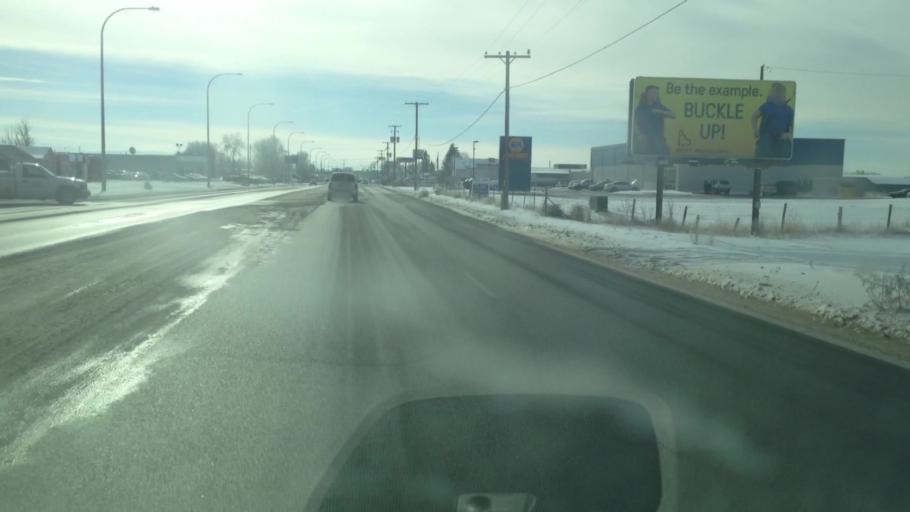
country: US
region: Idaho
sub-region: Bonneville County
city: Idaho Falls
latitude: 43.5190
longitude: -112.0236
